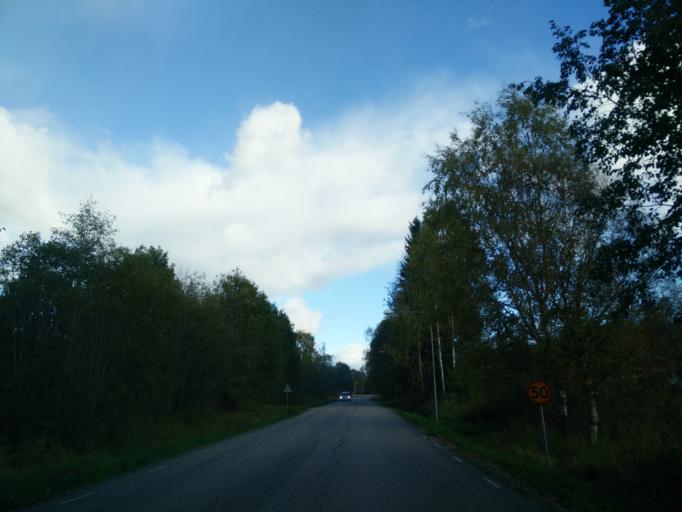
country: SE
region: Vaesternorrland
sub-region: Sundsvalls Kommun
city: Matfors
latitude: 62.3645
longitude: 17.0415
